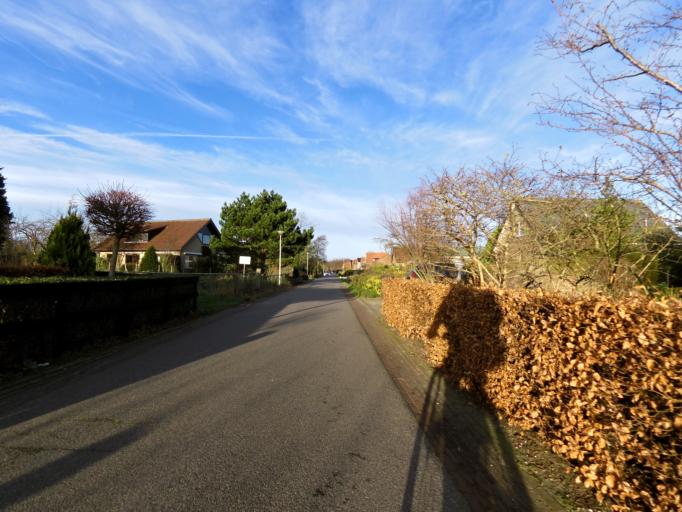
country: NL
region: South Holland
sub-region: Gemeente Brielle
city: Brielle
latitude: 51.9094
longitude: 4.0973
